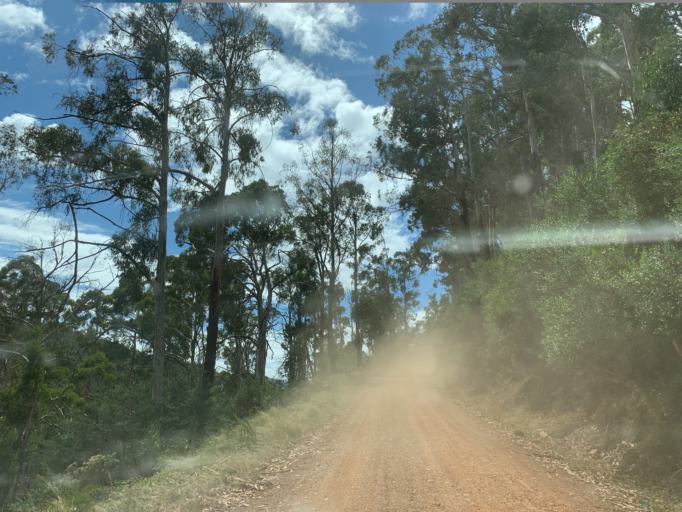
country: AU
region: Victoria
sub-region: Mansfield
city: Mansfield
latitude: -37.1010
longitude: 146.5039
